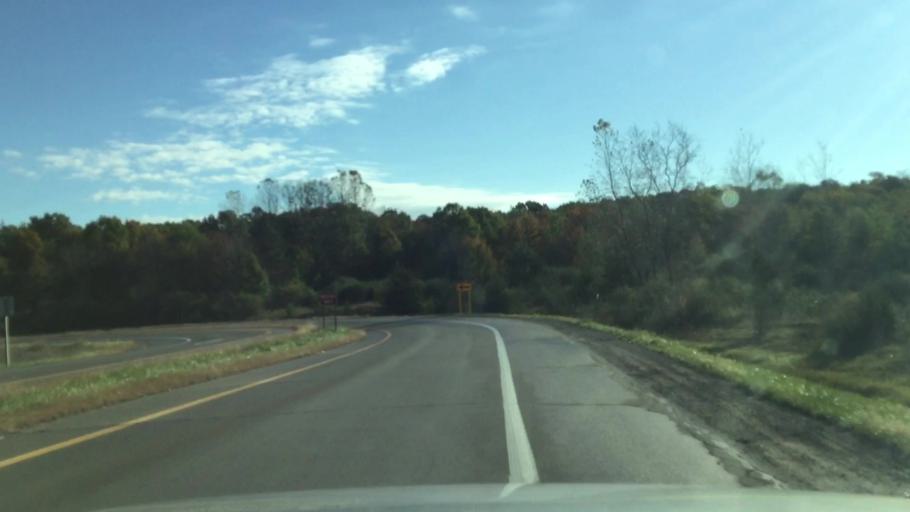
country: US
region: Michigan
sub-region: Shiawassee County
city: Durand
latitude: 42.9626
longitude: -83.9278
